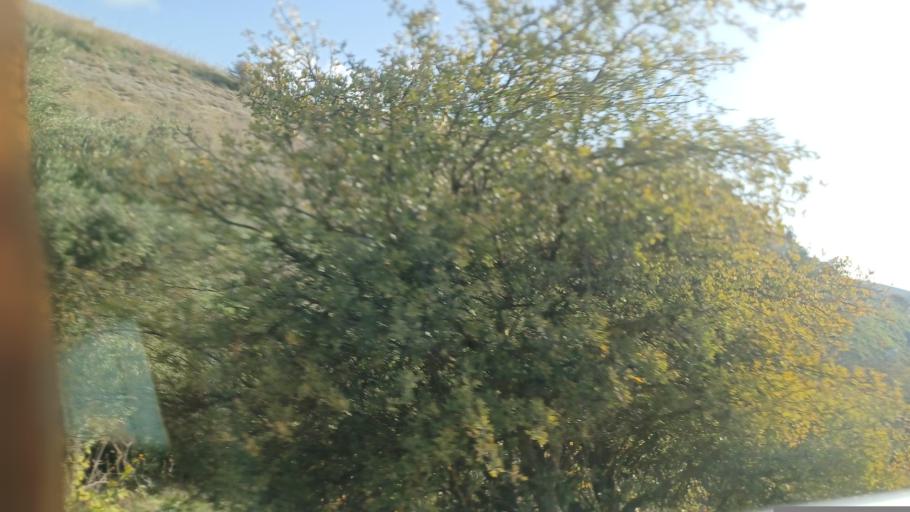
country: CY
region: Pafos
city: Mesogi
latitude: 34.8119
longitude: 32.4898
